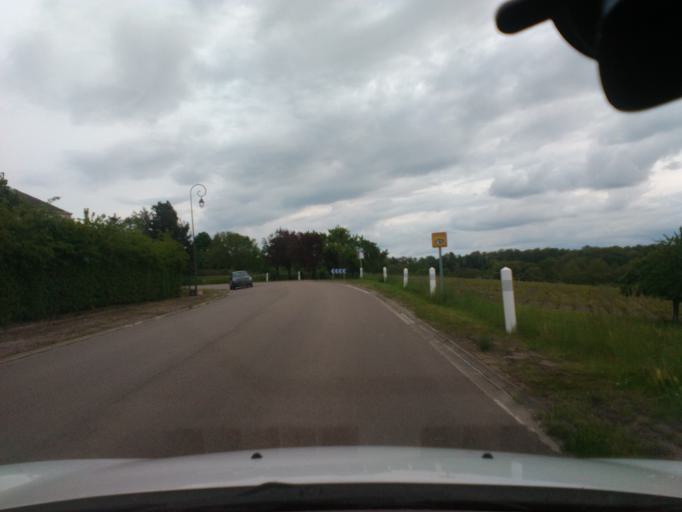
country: FR
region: Champagne-Ardenne
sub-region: Departement de l'Aube
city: Bar-sur-Aube
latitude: 48.2252
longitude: 4.8039
